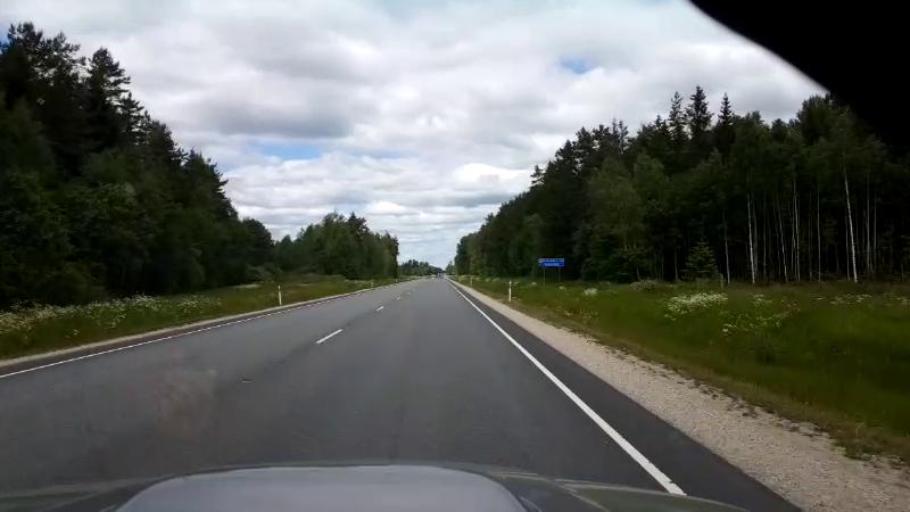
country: EE
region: Raplamaa
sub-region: Maerjamaa vald
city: Marjamaa
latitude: 58.8015
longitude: 24.4128
